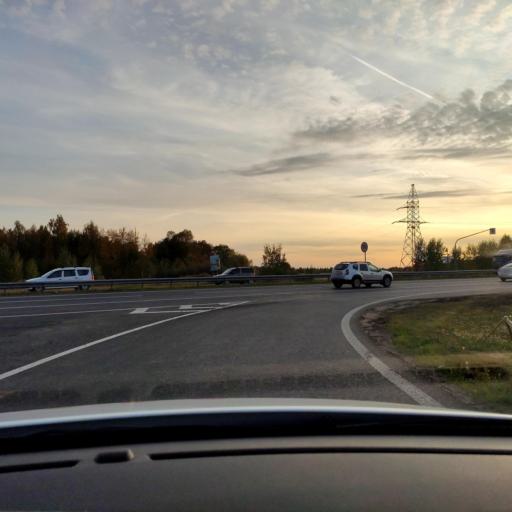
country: RU
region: Tatarstan
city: Pestretsy
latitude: 55.7235
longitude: 49.4561
